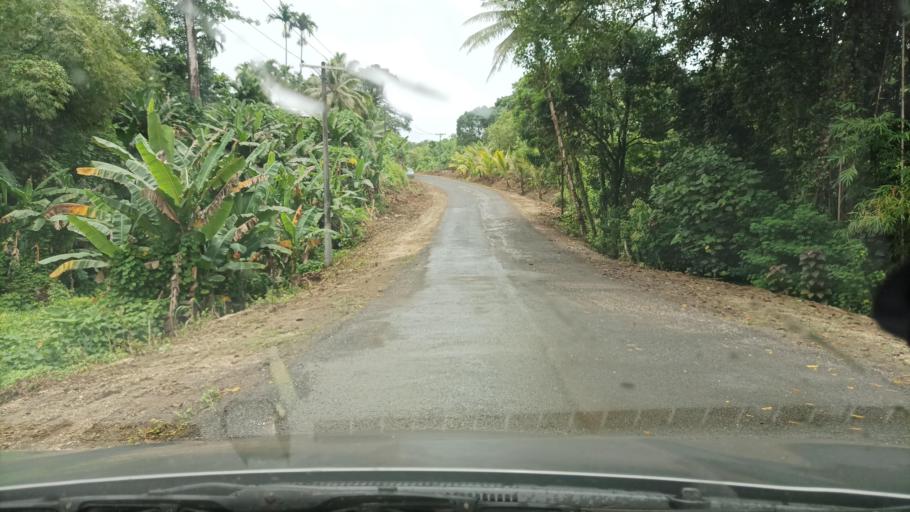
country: FM
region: Pohnpei
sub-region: Madolenihm Municipality
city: Madolenihm Municipality Government
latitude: 6.8148
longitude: 158.2353
